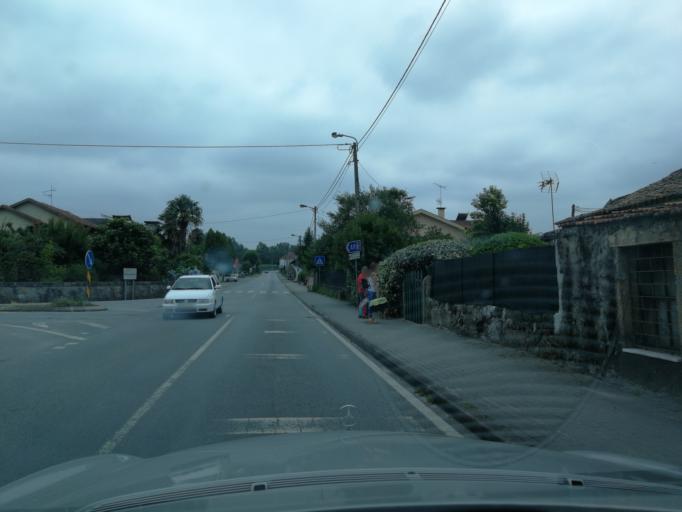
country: PT
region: Braga
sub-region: Vila Verde
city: Prado
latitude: 41.5934
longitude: -8.4611
